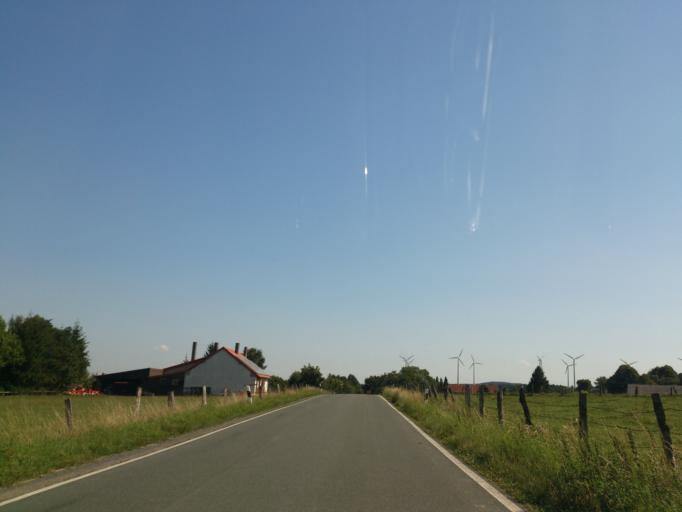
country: DE
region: North Rhine-Westphalia
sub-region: Regierungsbezirk Detmold
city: Willebadessen
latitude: 51.6520
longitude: 9.0445
